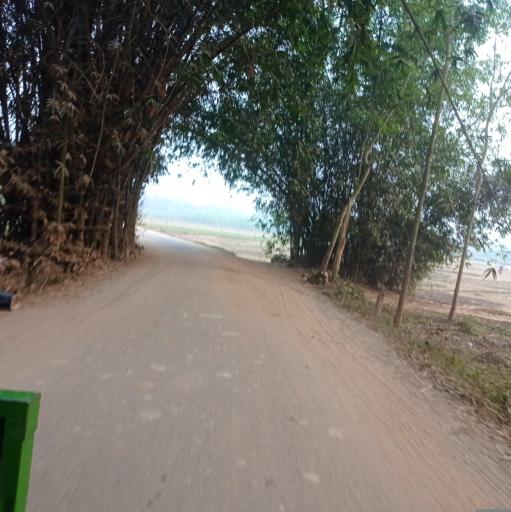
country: BD
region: Dhaka
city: Bajitpur
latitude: 24.1310
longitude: 90.8204
